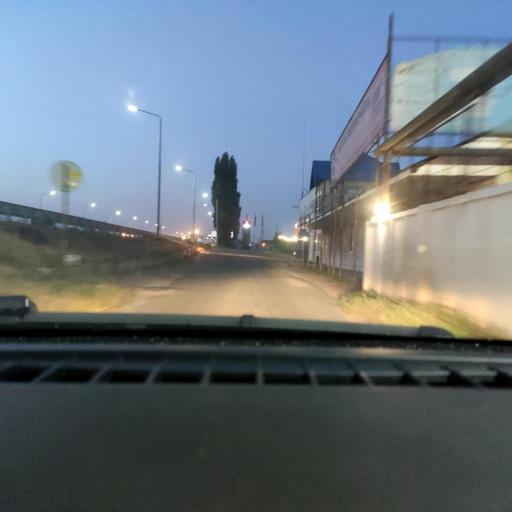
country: RU
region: Voronezj
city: Somovo
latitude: 51.6743
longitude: 39.3005
